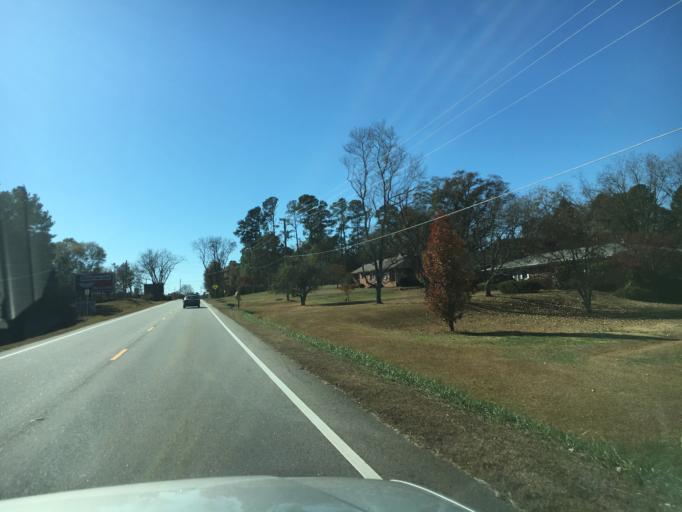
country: US
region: Georgia
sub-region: Hart County
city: Hartwell
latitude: 34.3436
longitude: -82.9466
